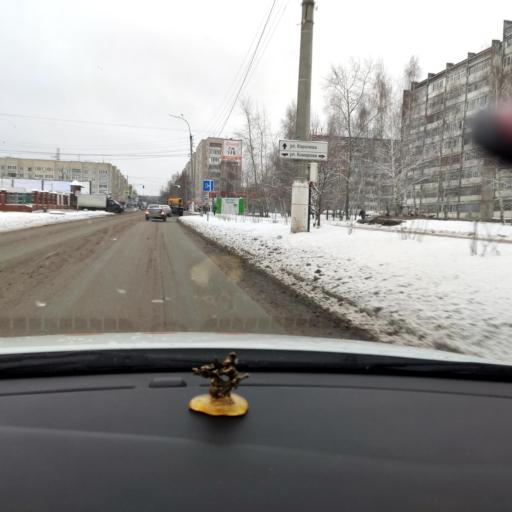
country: RU
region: Tatarstan
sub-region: Zelenodol'skiy Rayon
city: Zelenodolsk
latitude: 55.8574
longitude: 48.5589
